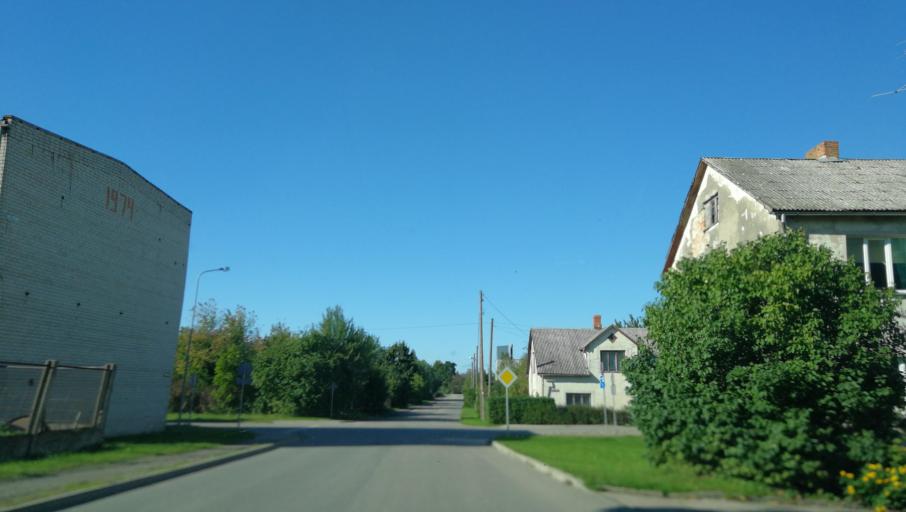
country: LV
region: Aizpute
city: Aizpute
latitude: 56.7239
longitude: 21.5954
